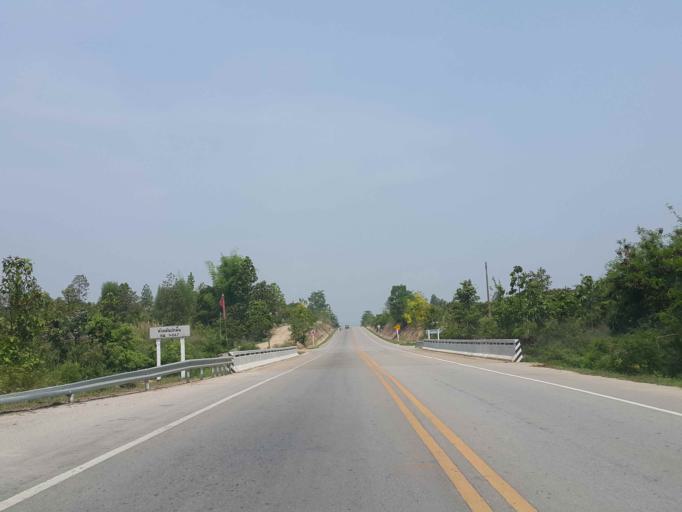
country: TH
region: Chiang Mai
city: Mae Taeng
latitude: 19.0745
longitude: 98.9293
